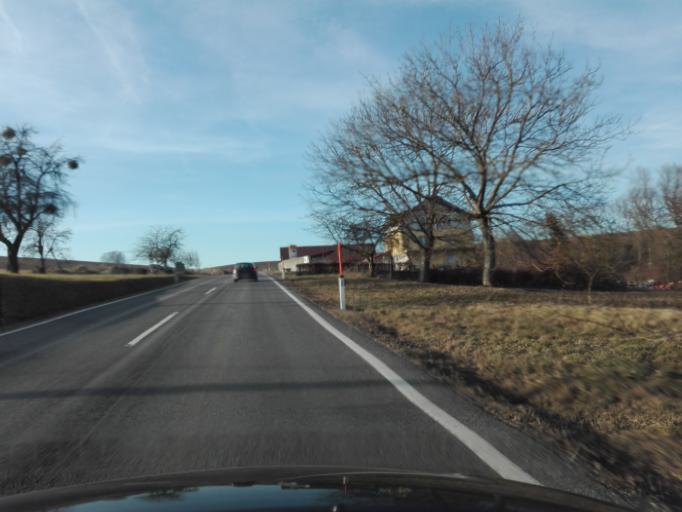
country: AT
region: Lower Austria
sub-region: Politischer Bezirk Amstetten
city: Sankt Valentin
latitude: 48.1813
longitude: 14.5746
